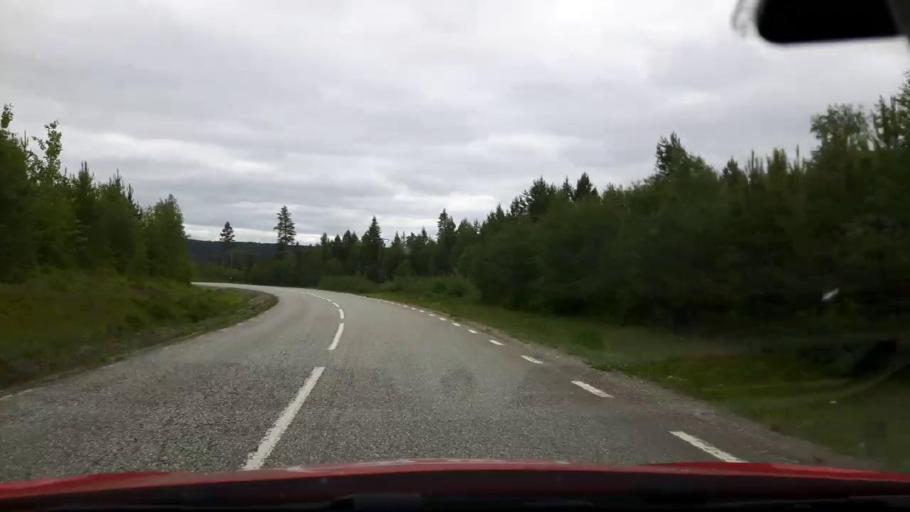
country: SE
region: Jaemtland
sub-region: Stroemsunds Kommun
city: Stroemsund
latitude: 63.3042
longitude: 15.7583
